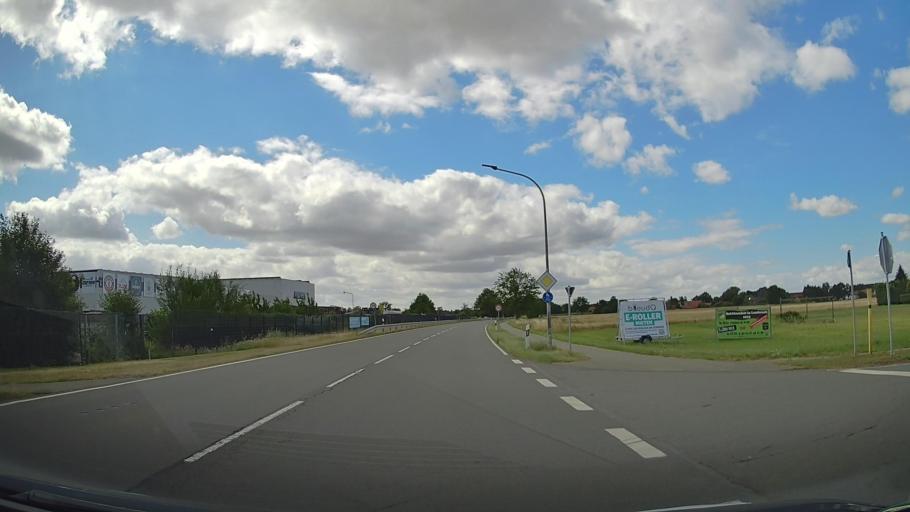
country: DE
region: Lower Saxony
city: Lembruch
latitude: 52.5297
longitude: 8.3764
